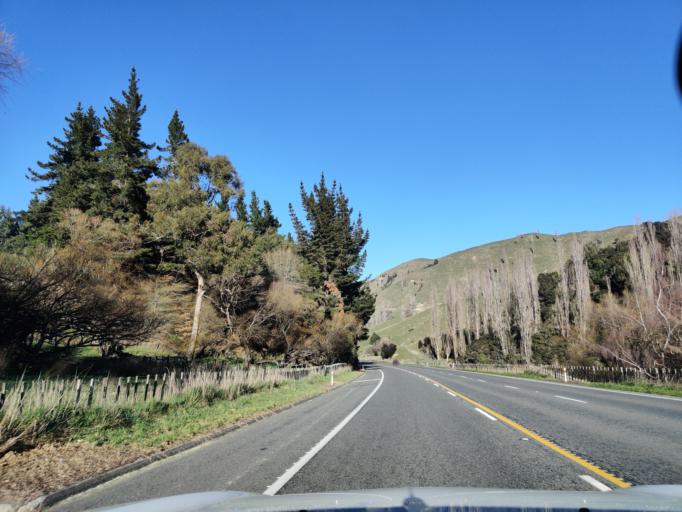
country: NZ
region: Manawatu-Wanganui
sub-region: Ruapehu District
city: Waiouru
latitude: -39.7749
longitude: 175.7906
